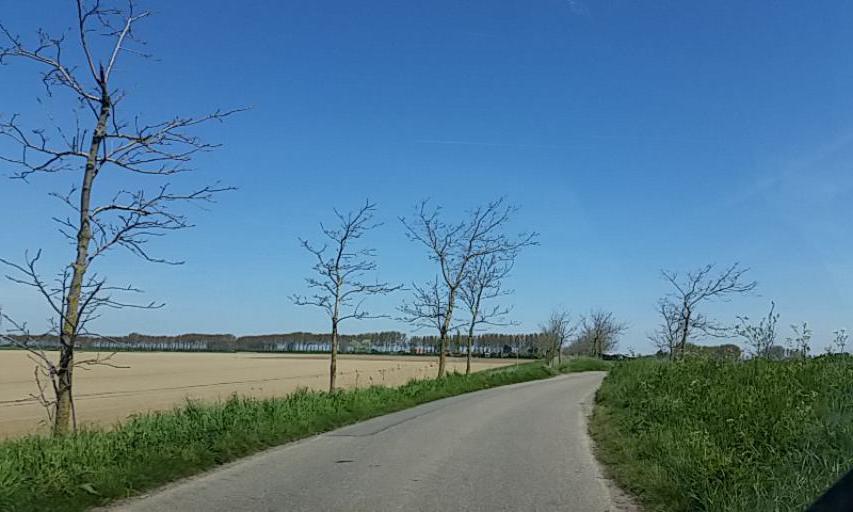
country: NL
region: Zeeland
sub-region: Gemeente Borsele
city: Borssele
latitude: 51.3342
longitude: 3.7094
